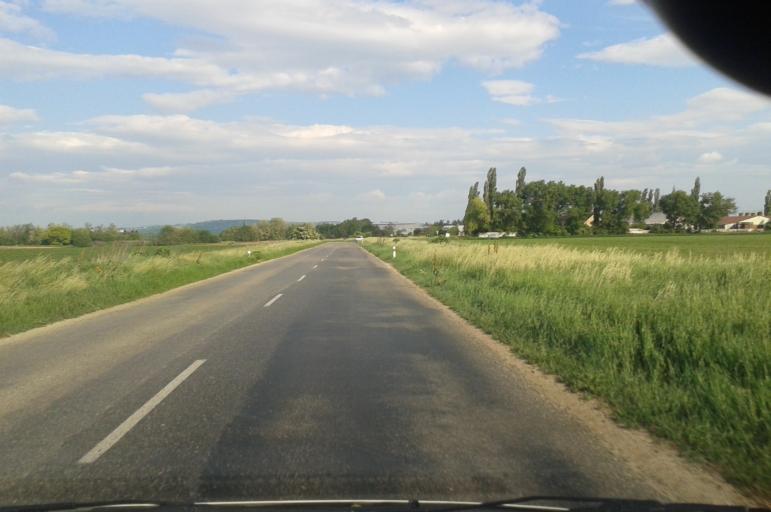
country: SK
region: Trnavsky
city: Leopoldov
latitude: 48.4423
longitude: 17.6966
